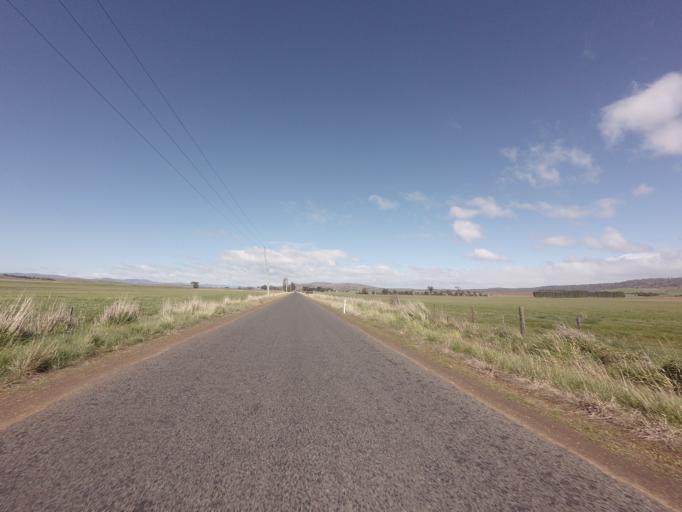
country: AU
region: Tasmania
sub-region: Northern Midlands
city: Evandale
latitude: -41.9952
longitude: 147.4541
